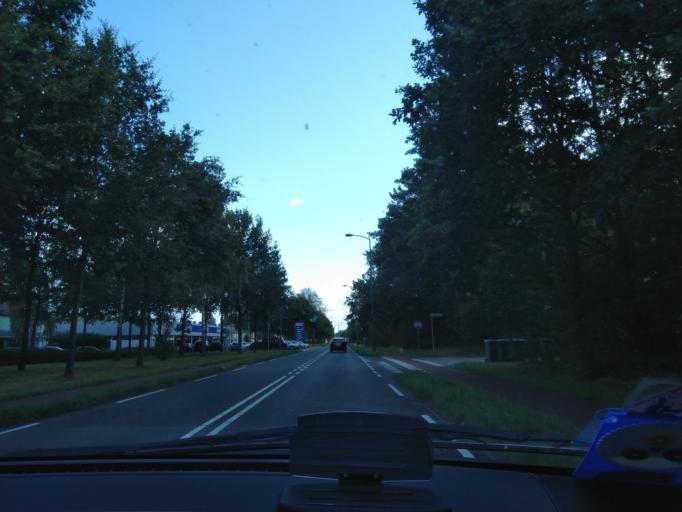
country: NL
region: North Brabant
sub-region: Gemeente Oosterhout
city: Oosterhout
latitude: 51.6219
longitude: 4.8622
